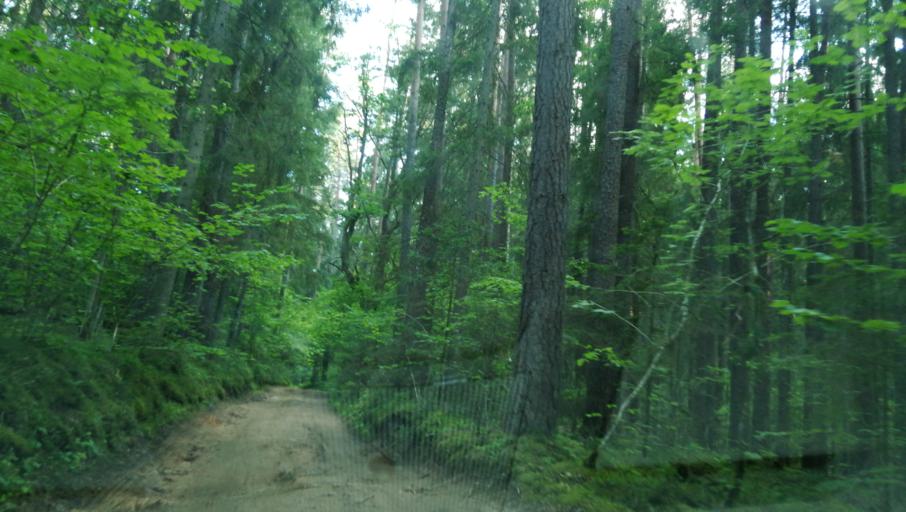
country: LV
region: Cesu Rajons
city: Cesis
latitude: 57.2830
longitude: 25.1769
